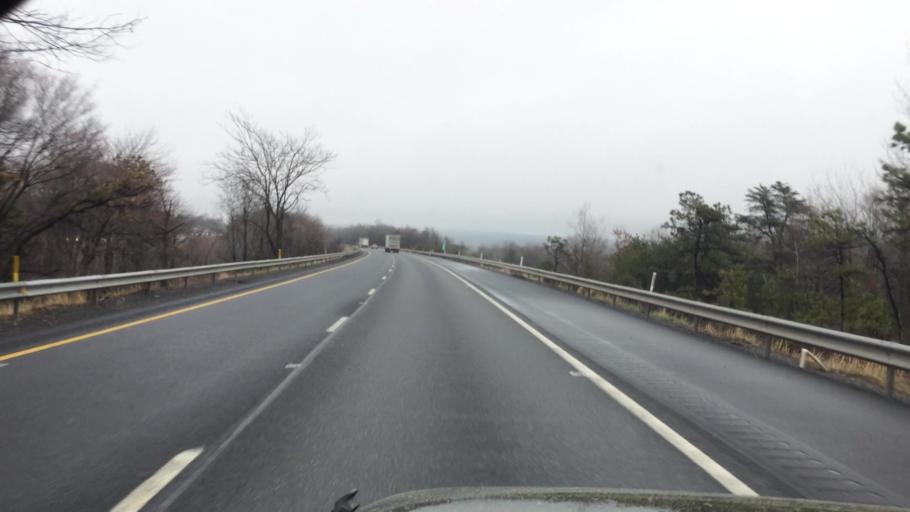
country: US
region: Pennsylvania
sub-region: Schuylkill County
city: Frackville
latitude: 40.7745
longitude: -76.2015
